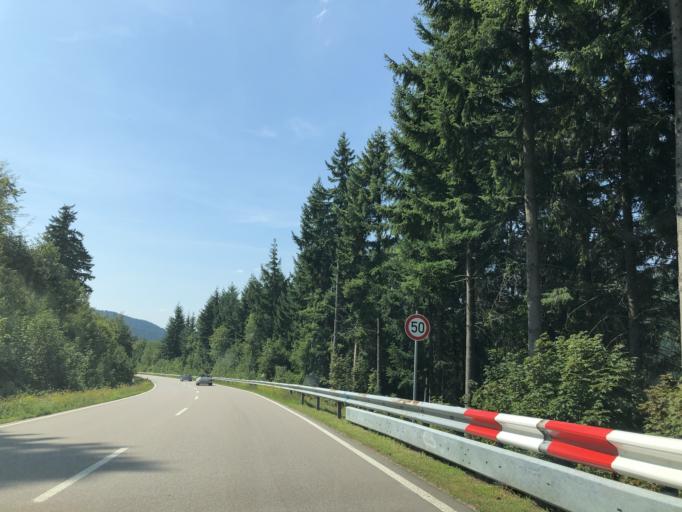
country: DE
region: Baden-Wuerttemberg
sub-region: Karlsruhe Region
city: Baden-Baden
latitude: 48.7156
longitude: 8.2369
